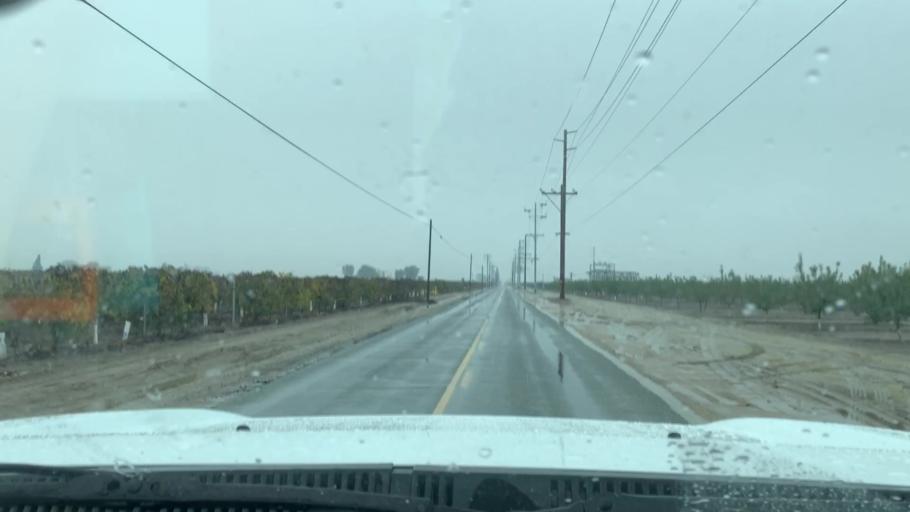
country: US
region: California
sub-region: Kern County
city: Delano
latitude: 35.8341
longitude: -119.2068
